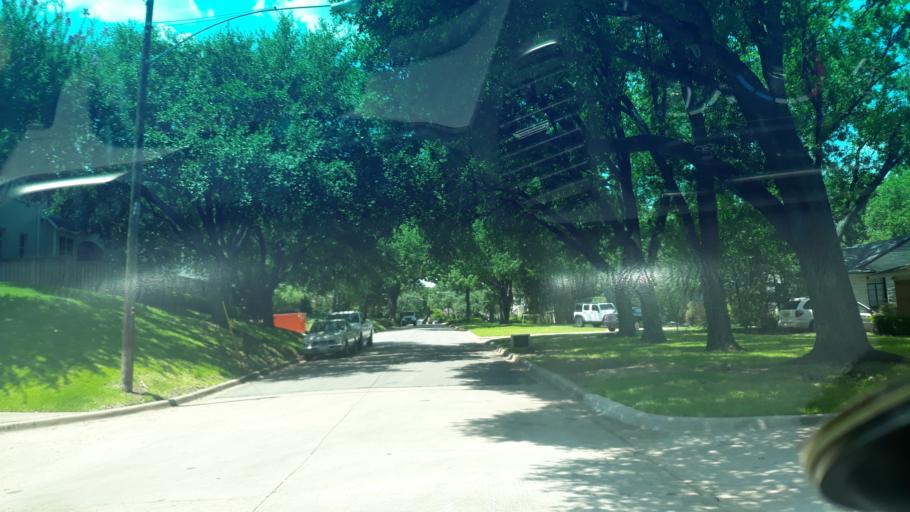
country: US
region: Texas
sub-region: Dallas County
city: Highland Park
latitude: 32.8258
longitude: -96.7368
